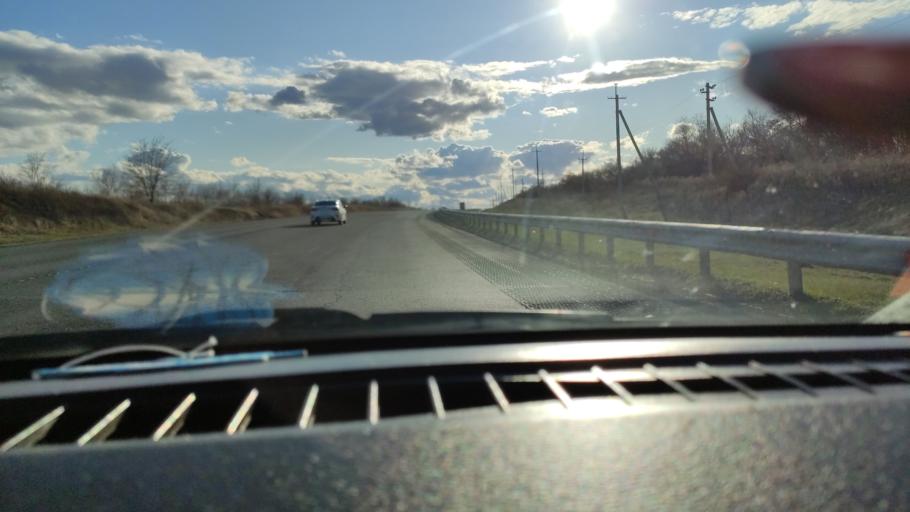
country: RU
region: Saratov
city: Shumeyka
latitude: 51.7770
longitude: 46.1097
